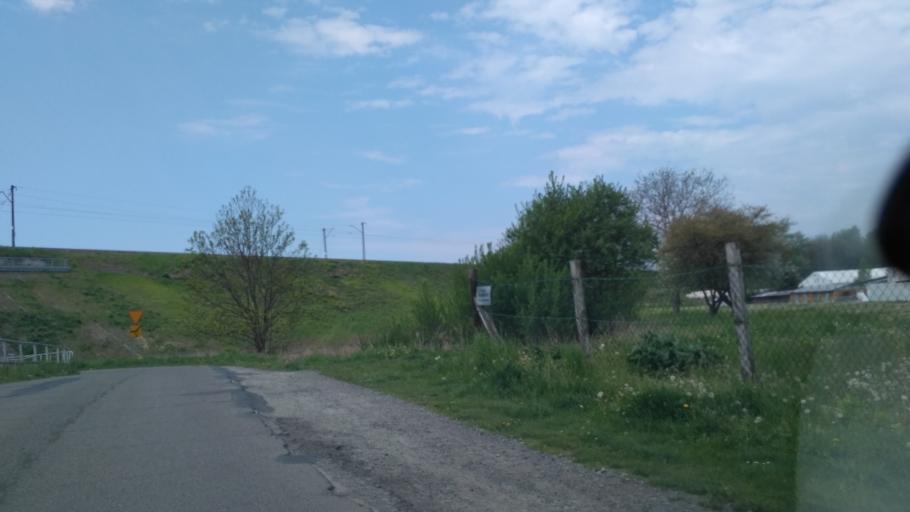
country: PL
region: Subcarpathian Voivodeship
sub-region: Powiat jaroslawski
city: Jaroslaw
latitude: 50.0139
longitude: 22.6650
